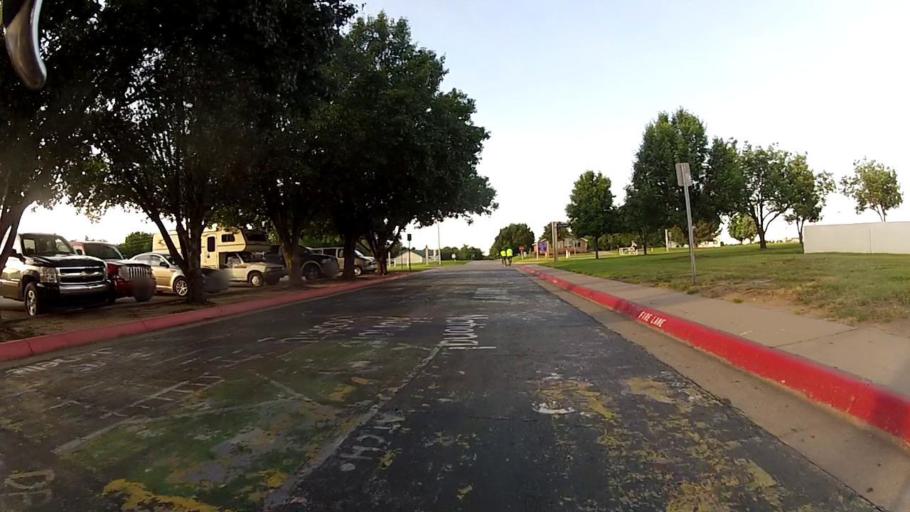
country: US
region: Kansas
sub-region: Cowley County
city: Arkansas City
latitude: 37.0863
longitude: -97.0529
